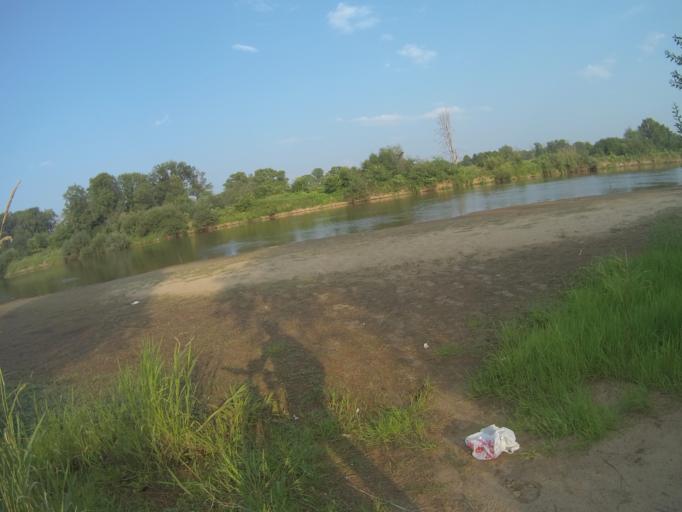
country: RU
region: Vladimir
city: Kommunar
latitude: 56.0903
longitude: 40.4143
